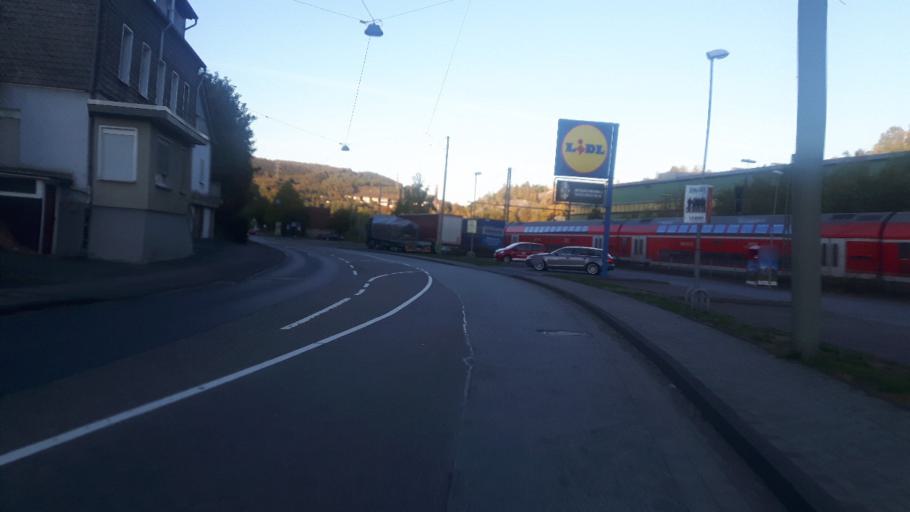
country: DE
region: Rheinland-Pfalz
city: Mudersbach
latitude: 50.8383
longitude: 7.9643
